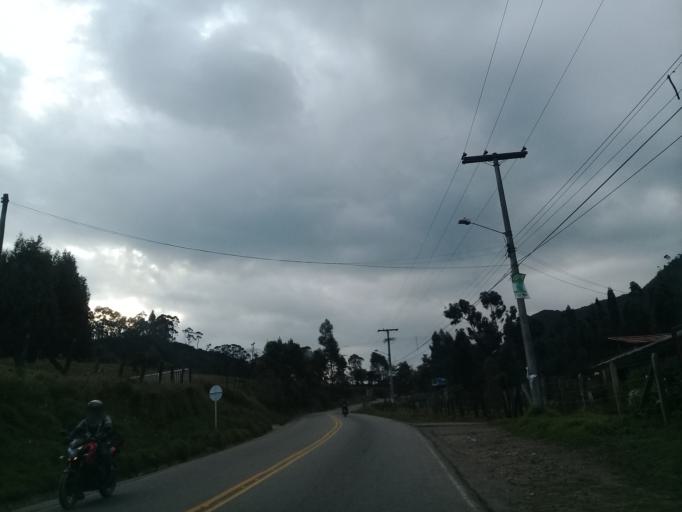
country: CO
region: Cundinamarca
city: Zipaquira
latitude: 5.0284
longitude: -74.0253
